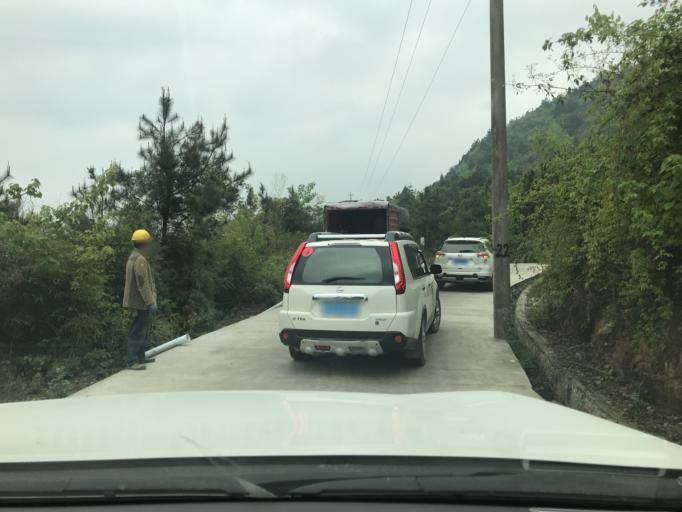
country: CN
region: Guizhou Sheng
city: Jiancha
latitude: 28.1789
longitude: 107.9985
